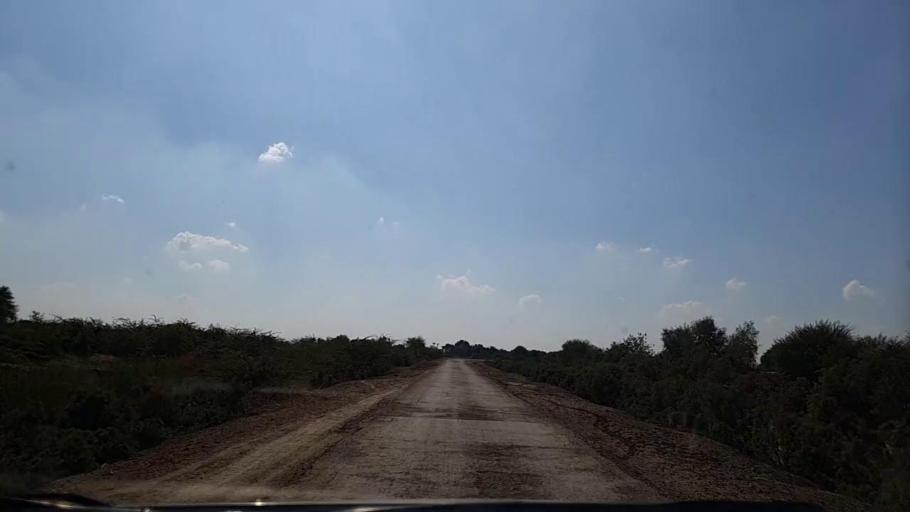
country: PK
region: Sindh
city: Pithoro
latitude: 25.6702
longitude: 69.4770
